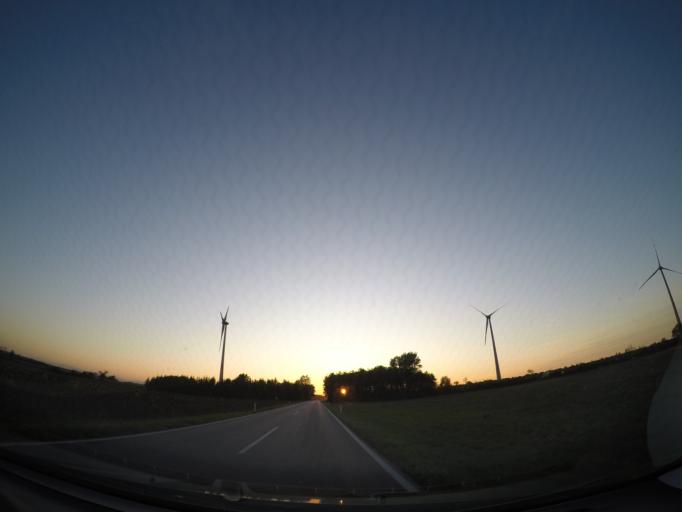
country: AT
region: Lower Austria
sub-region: Politischer Bezirk Baden
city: Seibersdorf
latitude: 47.9598
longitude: 16.4942
